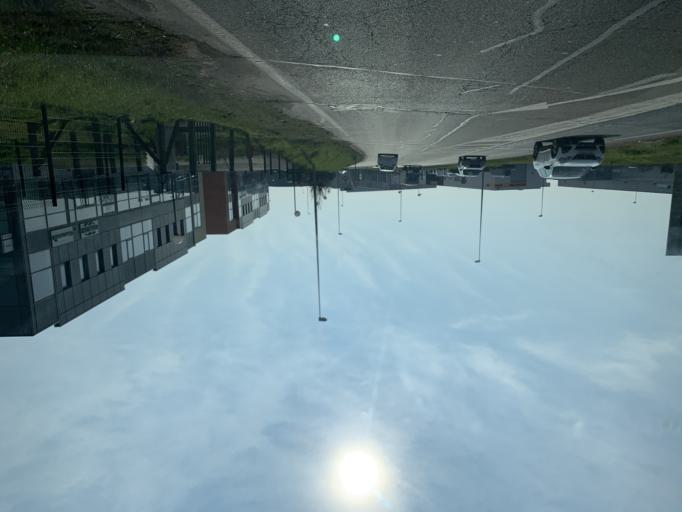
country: FR
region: Rhone-Alpes
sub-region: Departement du Rhone
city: Arnas
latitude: 46.0174
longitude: 4.7239
